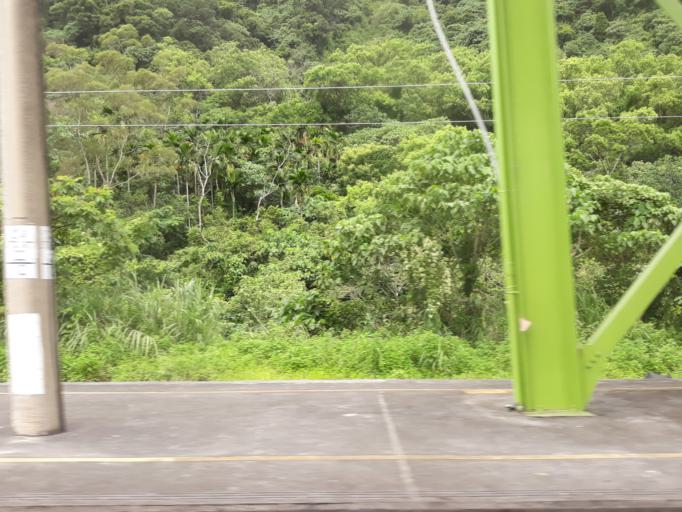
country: TW
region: Taiwan
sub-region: Yilan
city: Yilan
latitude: 24.4489
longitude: 121.7757
